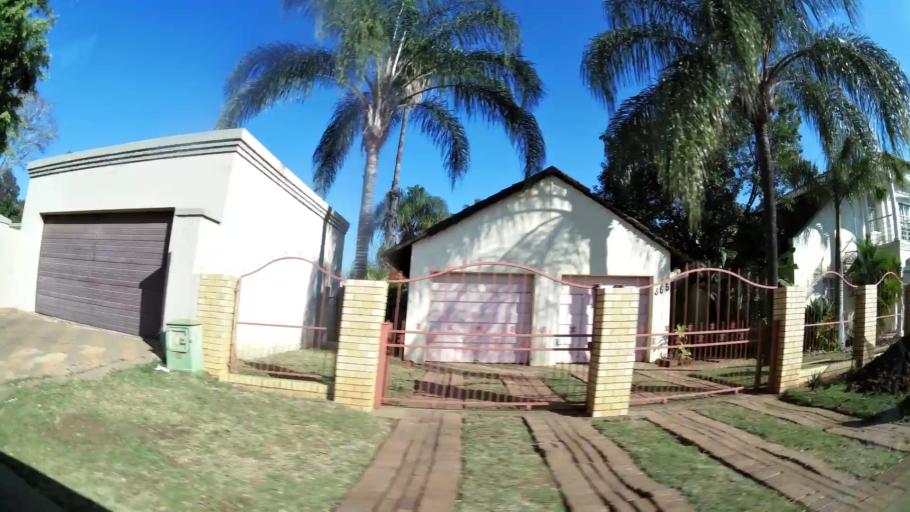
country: ZA
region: Gauteng
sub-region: City of Tshwane Metropolitan Municipality
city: Pretoria
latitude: -25.6737
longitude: 28.2335
